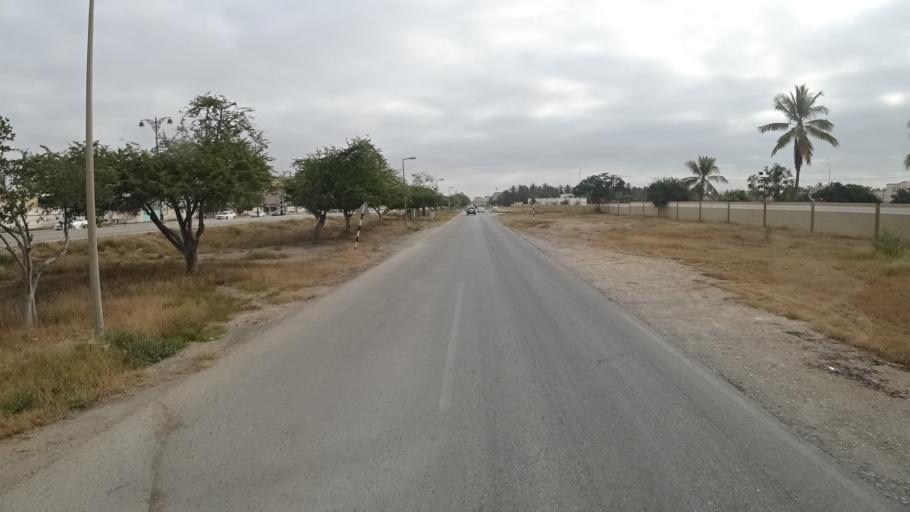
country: OM
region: Zufar
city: Salalah
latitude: 17.0114
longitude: 54.0479
